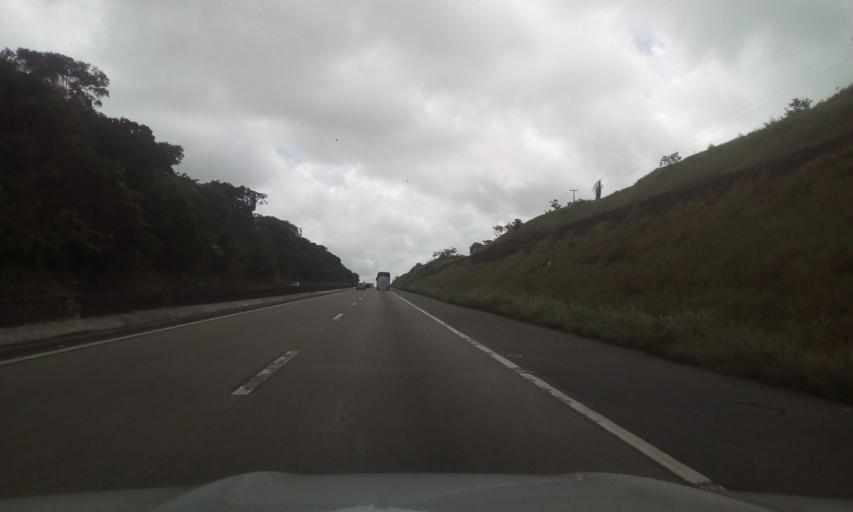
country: BR
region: Pernambuco
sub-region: Itapissuma
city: Itapissuma
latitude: -7.6846
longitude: -34.9234
